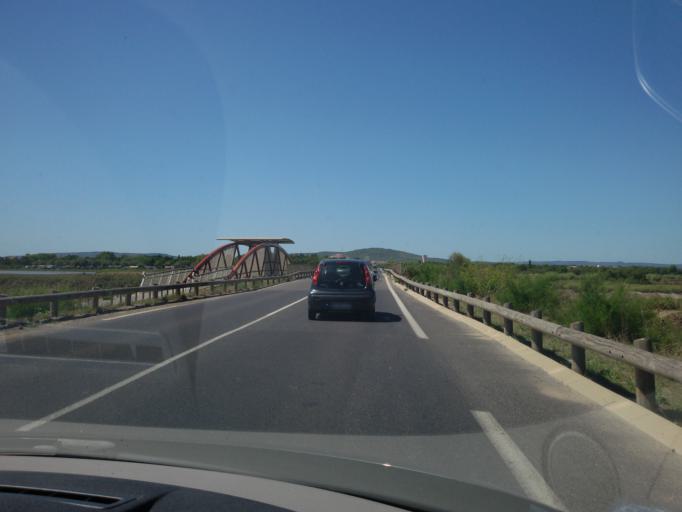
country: FR
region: Languedoc-Roussillon
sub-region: Departement de l'Herault
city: Villeneuve-les-Maguelone
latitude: 43.5393
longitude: 3.8800
